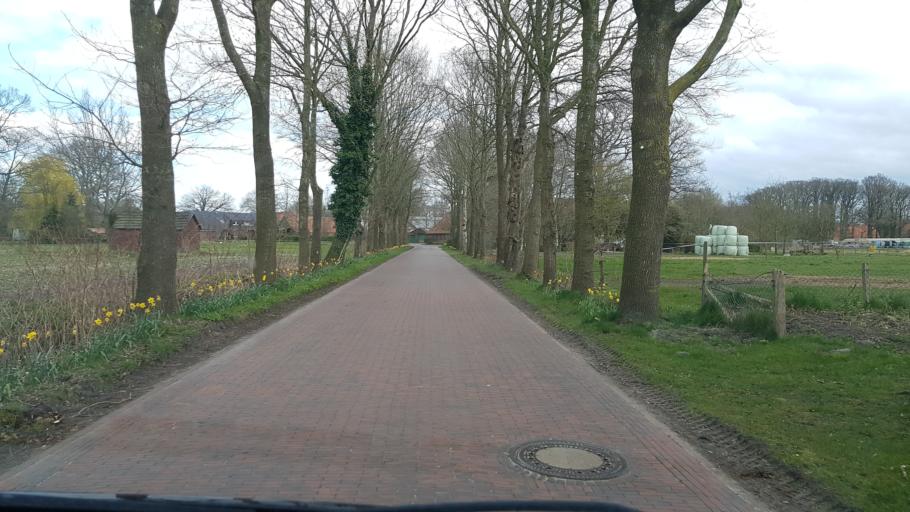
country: DE
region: Lower Saxony
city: Edewecht
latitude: 53.1162
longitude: 7.9404
